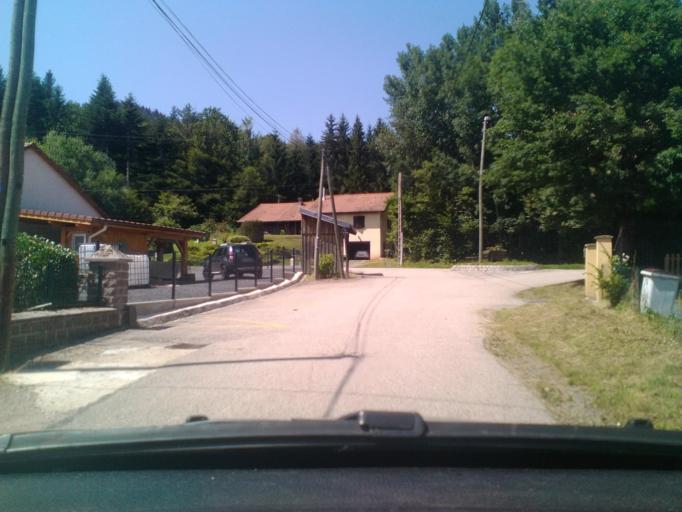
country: FR
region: Lorraine
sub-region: Departement des Vosges
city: Senones
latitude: 48.3863
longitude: 6.9455
